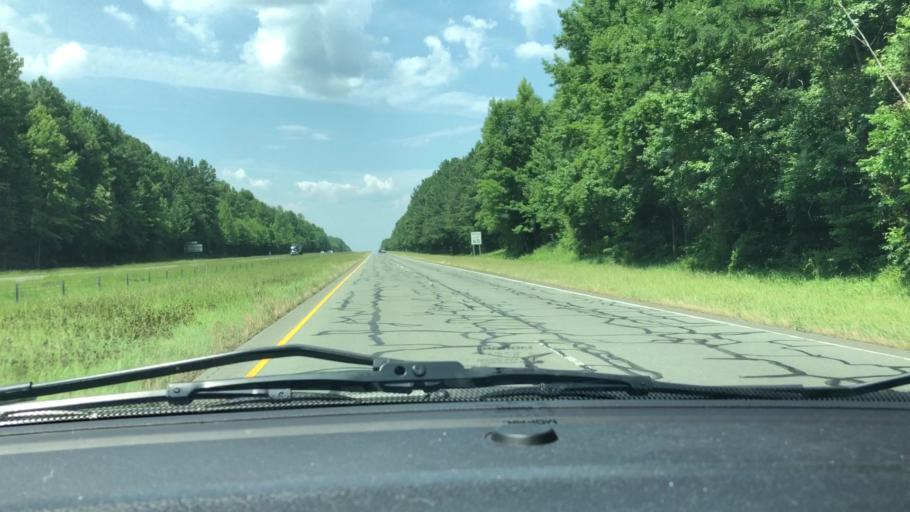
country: US
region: North Carolina
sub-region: Chatham County
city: Siler City
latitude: 35.7040
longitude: -79.4286
